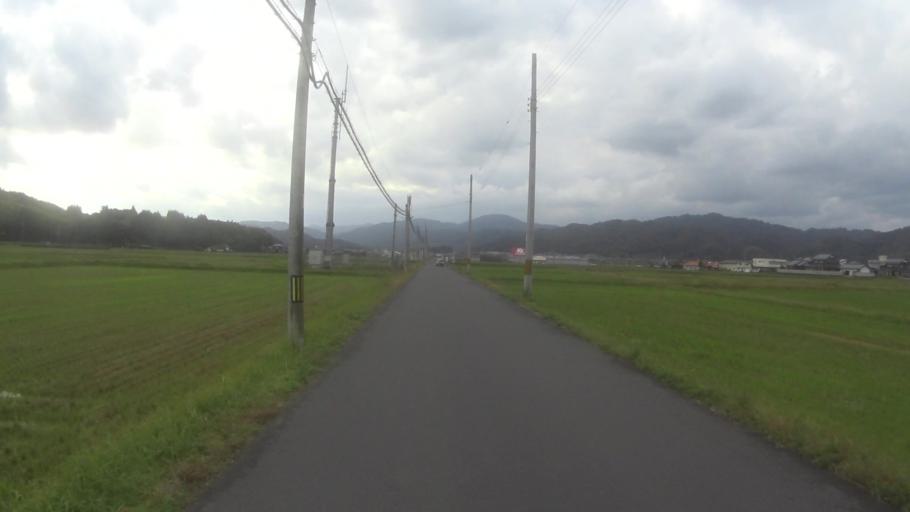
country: JP
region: Kyoto
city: Miyazu
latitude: 35.5272
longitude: 135.1264
